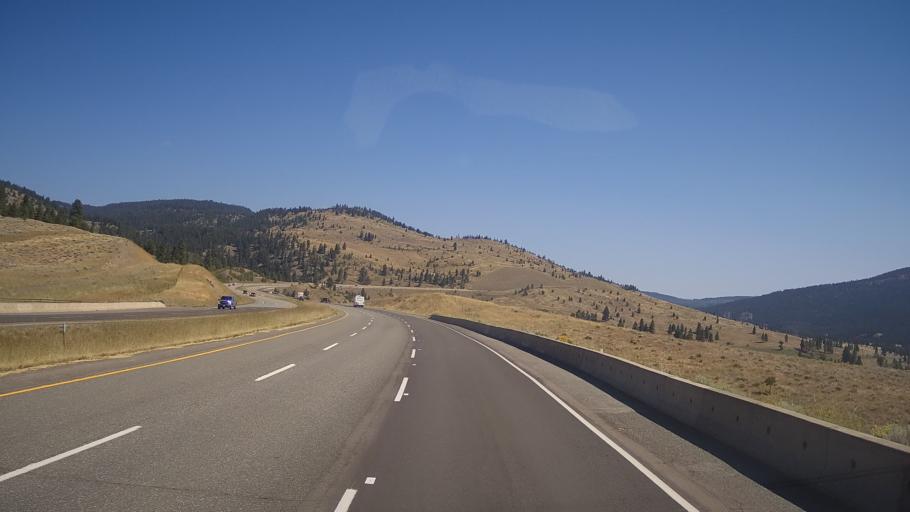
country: CA
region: British Columbia
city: Merritt
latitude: 50.1849
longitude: -120.6809
